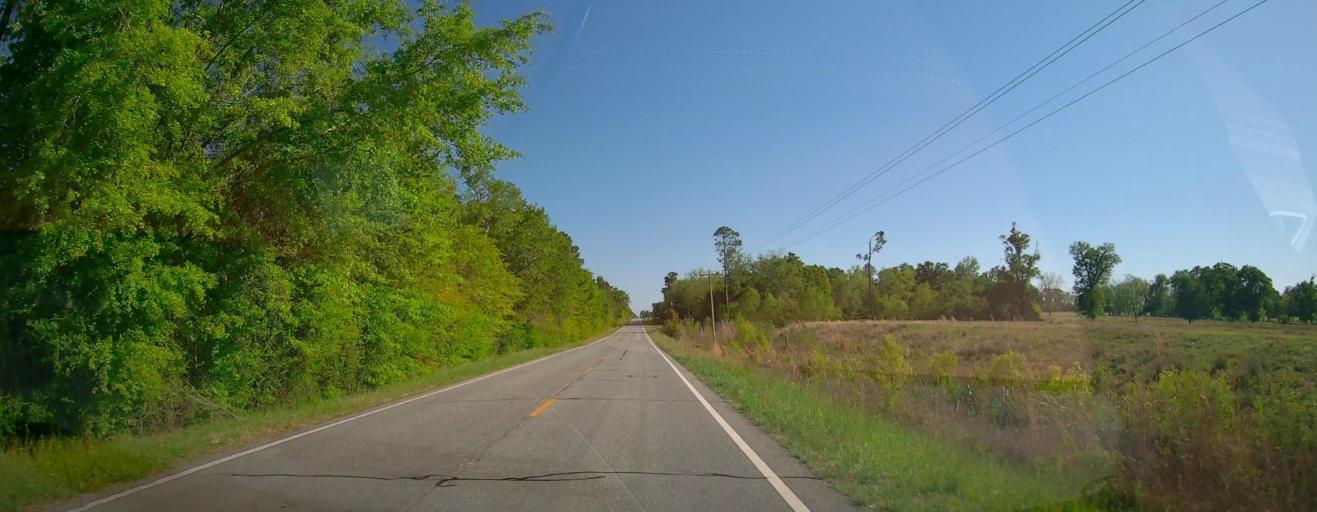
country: US
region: Georgia
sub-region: Wilcox County
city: Rochelle
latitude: 31.8750
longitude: -83.4888
